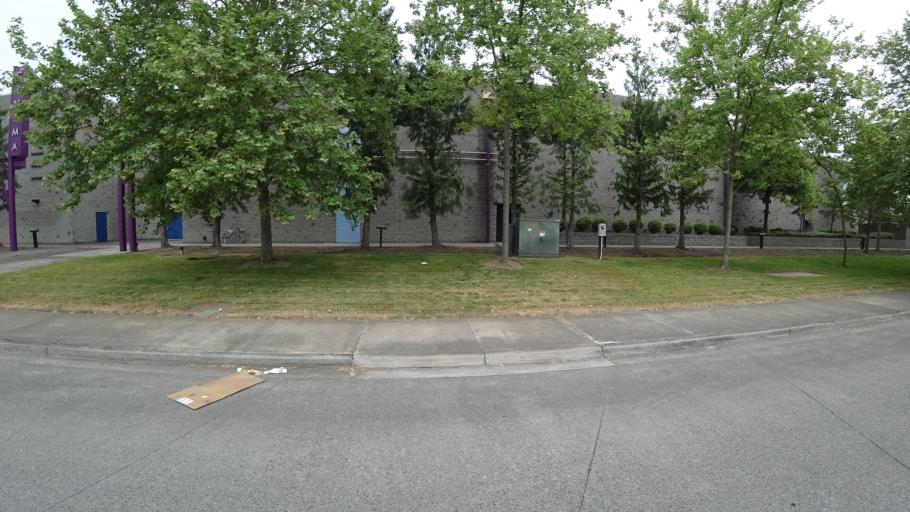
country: US
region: Oregon
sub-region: Washington County
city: Aloha
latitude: 45.4973
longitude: -122.9200
